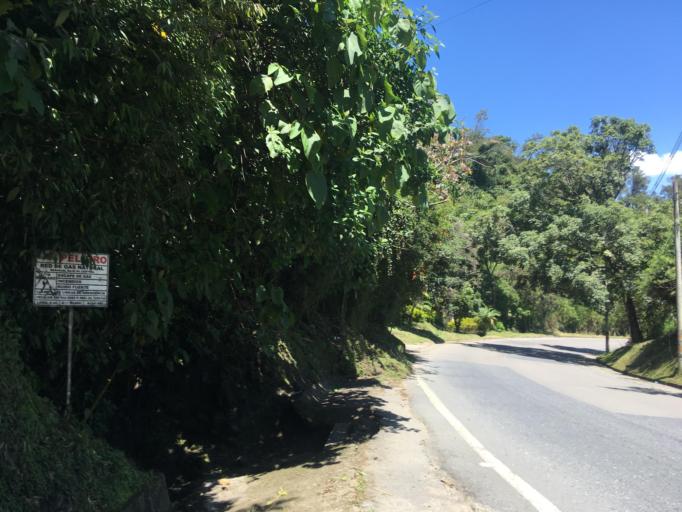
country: CO
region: Santander
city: Barbosa
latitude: 5.9175
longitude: -73.5995
